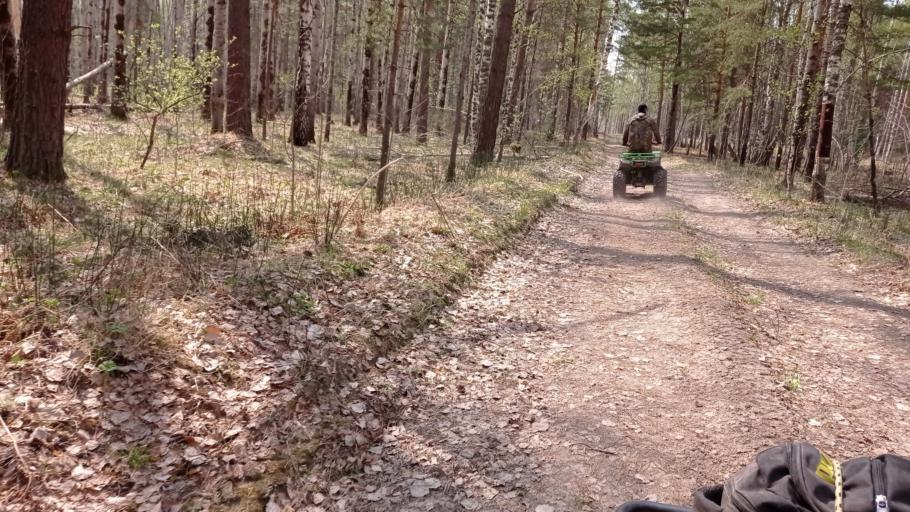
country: RU
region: Tomsk
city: Timiryazevskoye
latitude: 56.4353
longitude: 84.6484
